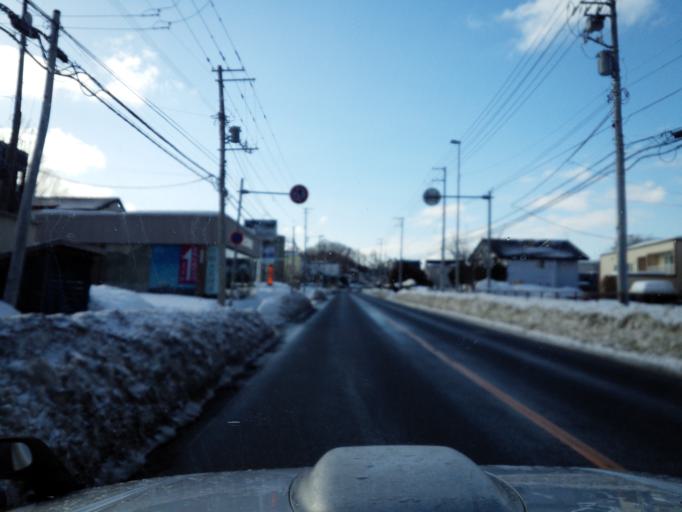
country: JP
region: Hokkaido
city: Sapporo
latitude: 42.9480
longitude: 141.3469
